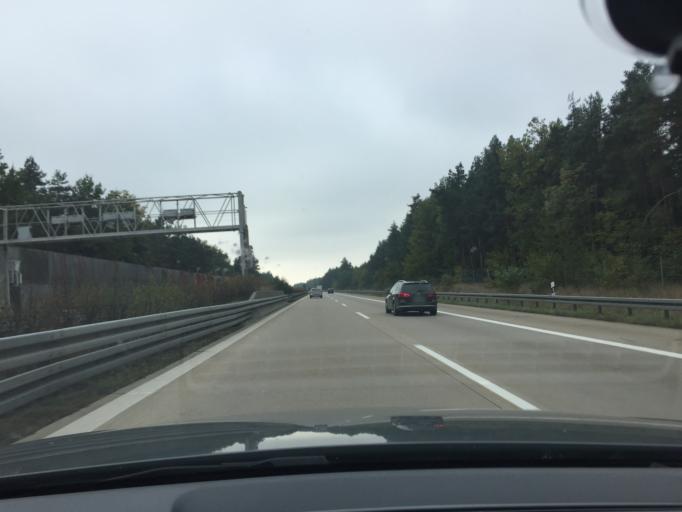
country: DE
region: Brandenburg
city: Ruhland
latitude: 51.4525
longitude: 13.8456
